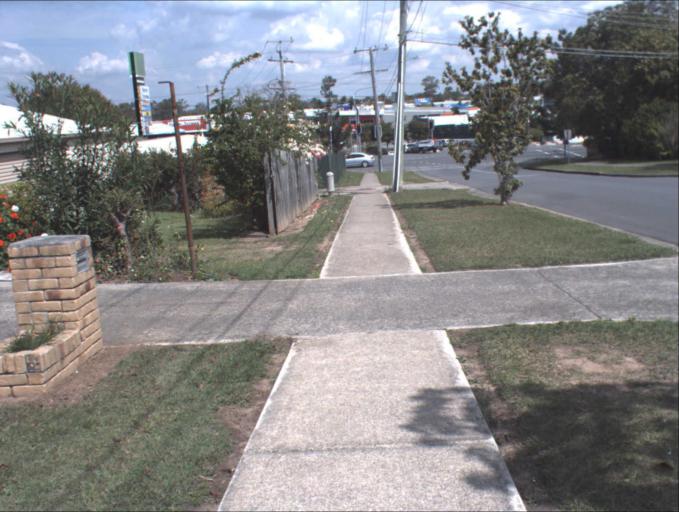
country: AU
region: Queensland
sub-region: Brisbane
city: Sunnybank Hills
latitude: -27.6609
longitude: 153.0461
